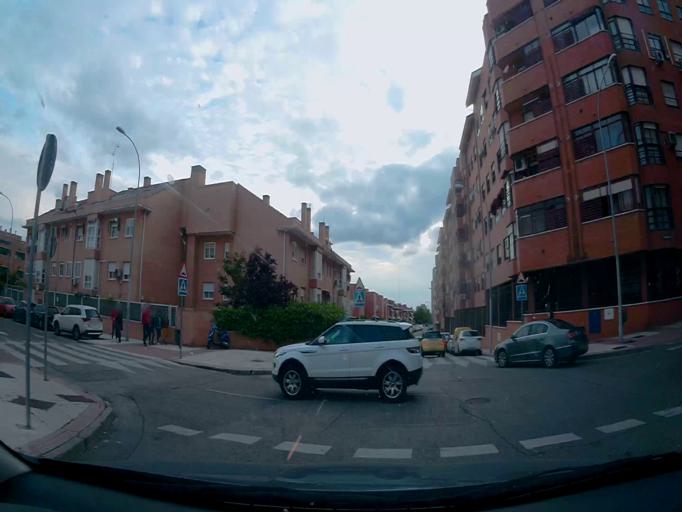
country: ES
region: Madrid
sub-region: Provincia de Madrid
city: Alcorcon
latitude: 40.3370
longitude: -3.8282
